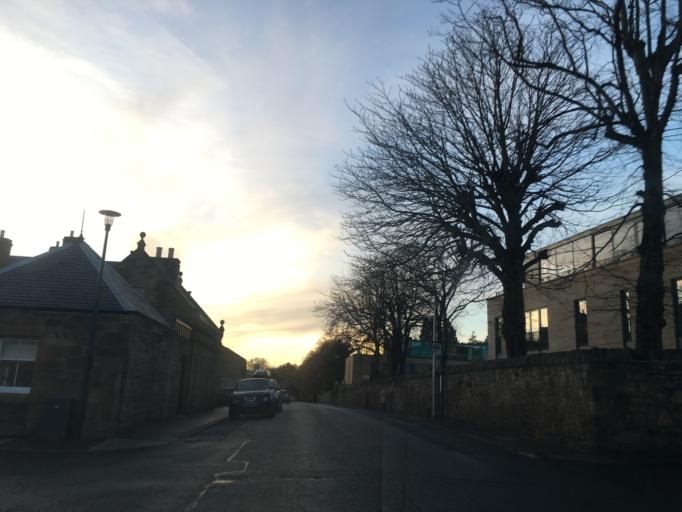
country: GB
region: Scotland
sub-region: Edinburgh
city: Colinton
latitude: 55.9469
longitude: -3.2470
